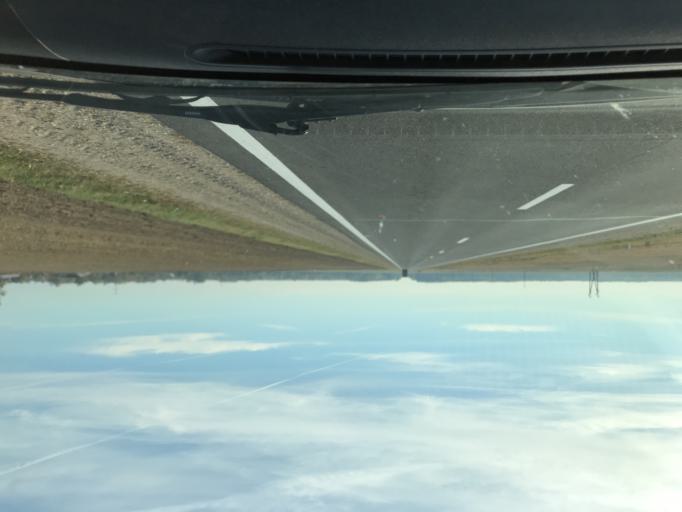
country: BY
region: Brest
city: Horad Pinsk
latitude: 52.1492
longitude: 25.8757
